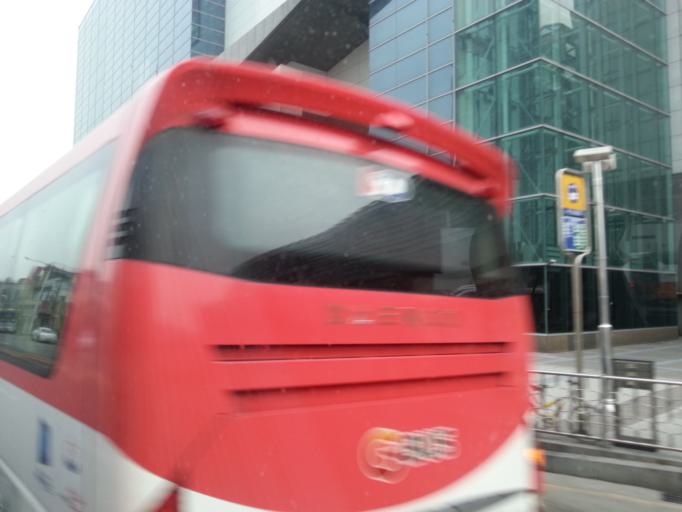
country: KR
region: Gyeonggi-do
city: Anyang-si
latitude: 37.4014
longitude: 126.9223
